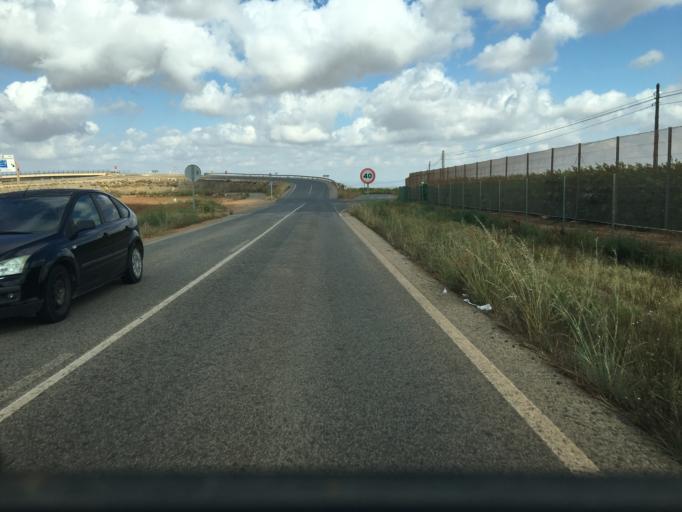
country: ES
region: Murcia
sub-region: Murcia
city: La Union
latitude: 37.6504
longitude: -0.8811
